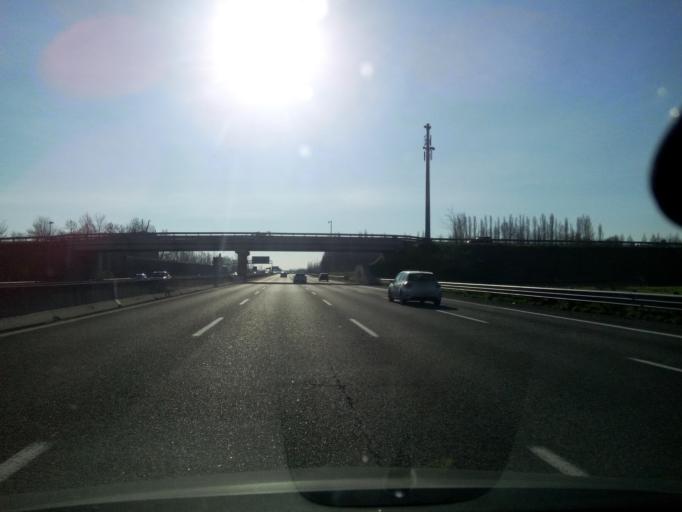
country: IT
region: Emilia-Romagna
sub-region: Provincia di Modena
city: San Vito
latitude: 44.5787
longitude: 10.9815
